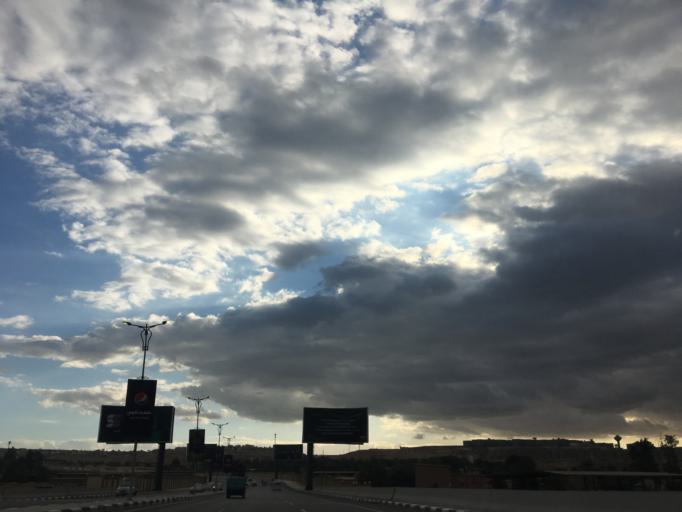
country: EG
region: Muhafazat al Qahirah
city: Cairo
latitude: 30.0410
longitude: 31.3073
